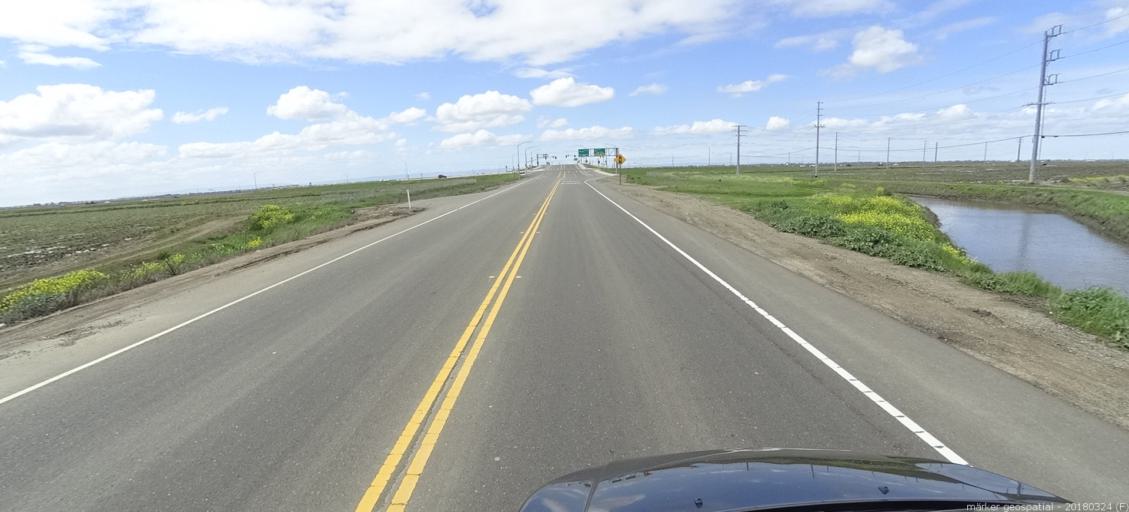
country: US
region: California
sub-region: Sacramento County
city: Elverta
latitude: 38.7143
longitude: -121.5348
